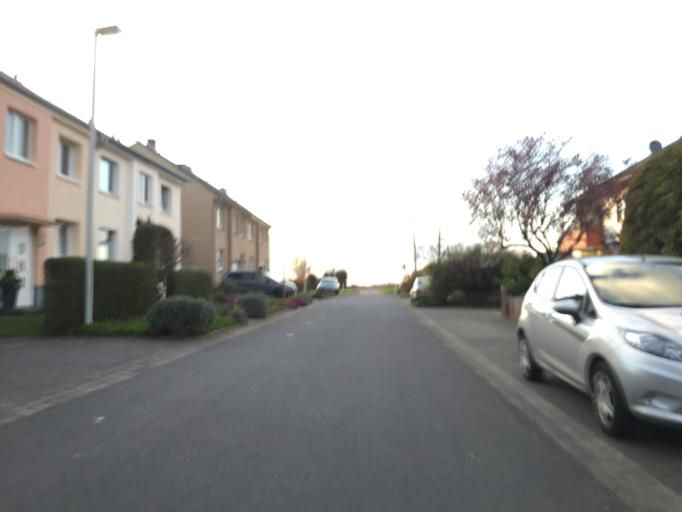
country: DE
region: North Rhine-Westphalia
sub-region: Regierungsbezirk Koln
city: Bonn
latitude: 50.7267
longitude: 7.0632
